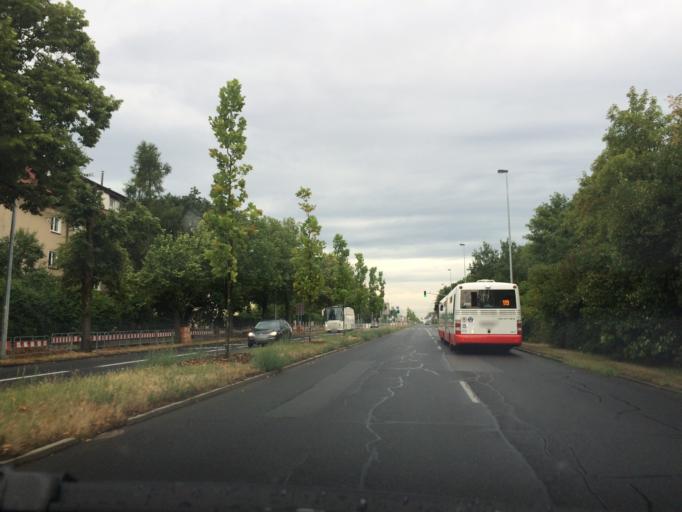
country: CZ
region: Central Bohemia
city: Horomerice
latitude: 50.0929
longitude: 14.3169
